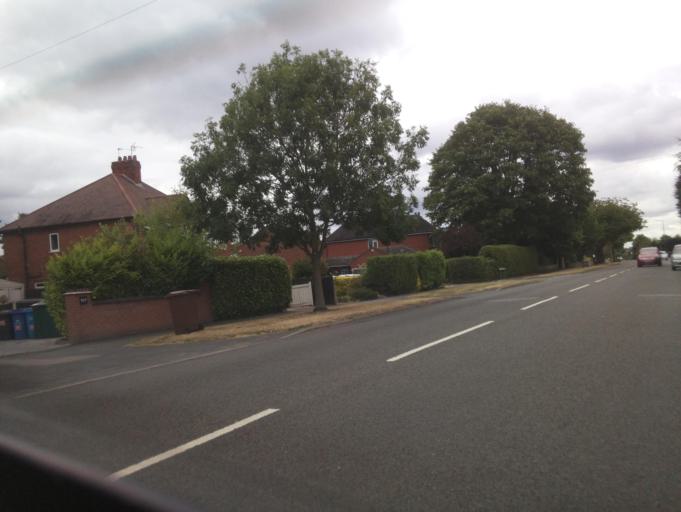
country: GB
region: England
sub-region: Derbyshire
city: Long Eaton
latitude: 52.8981
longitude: -1.3080
